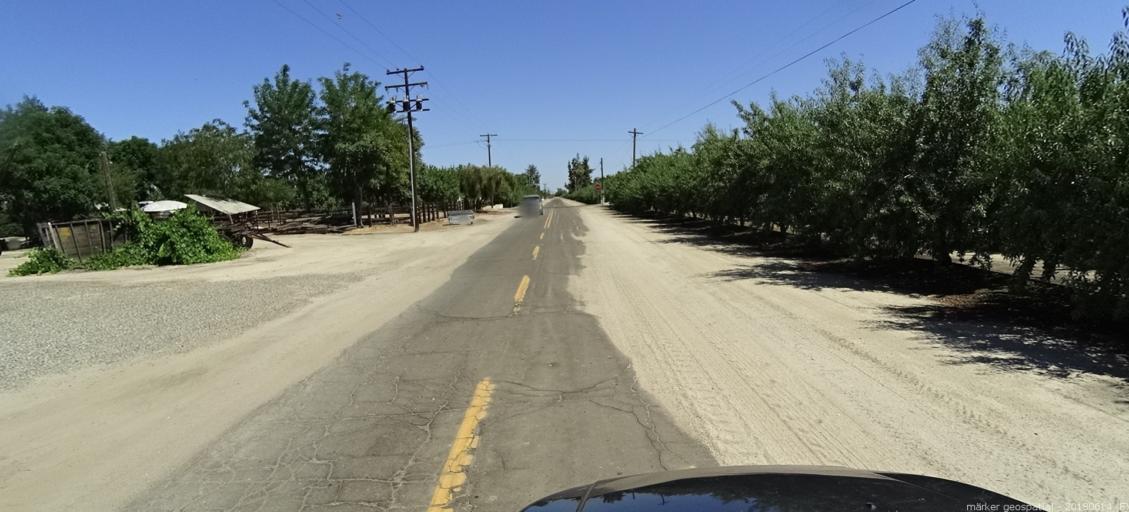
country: US
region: California
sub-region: Madera County
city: Fairmead
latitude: 36.9884
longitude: -120.1842
